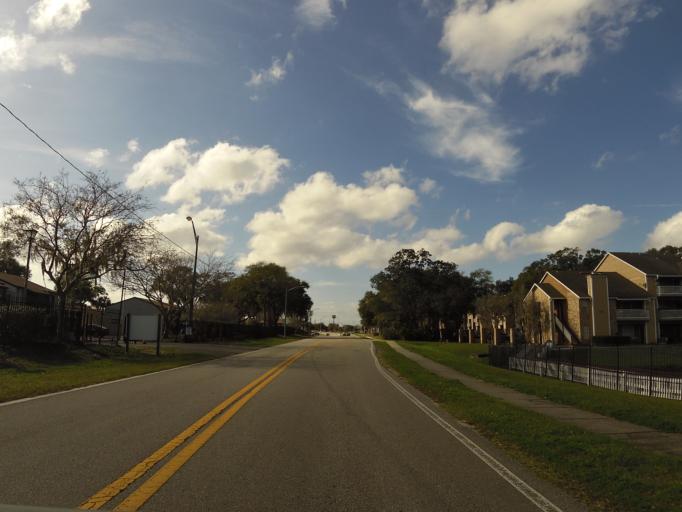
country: US
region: Florida
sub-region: Duval County
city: Jacksonville
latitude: 30.3307
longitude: -81.5443
